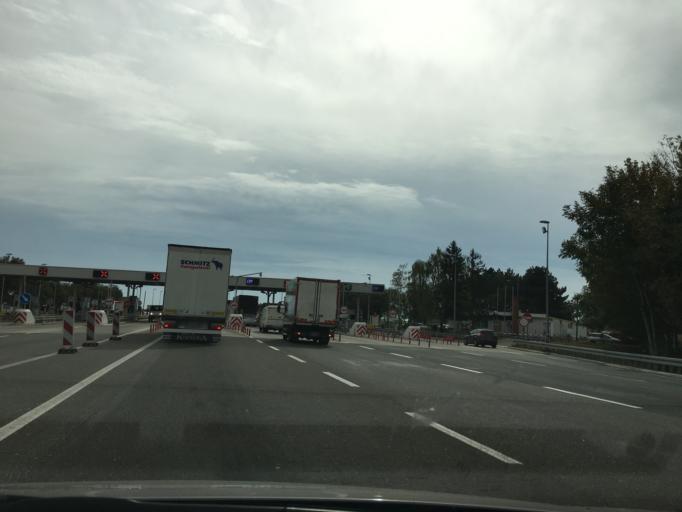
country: RS
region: Autonomna Pokrajina Vojvodina
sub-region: Sremski Okrug
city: Stara Pazova
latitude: 45.0071
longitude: 20.2010
